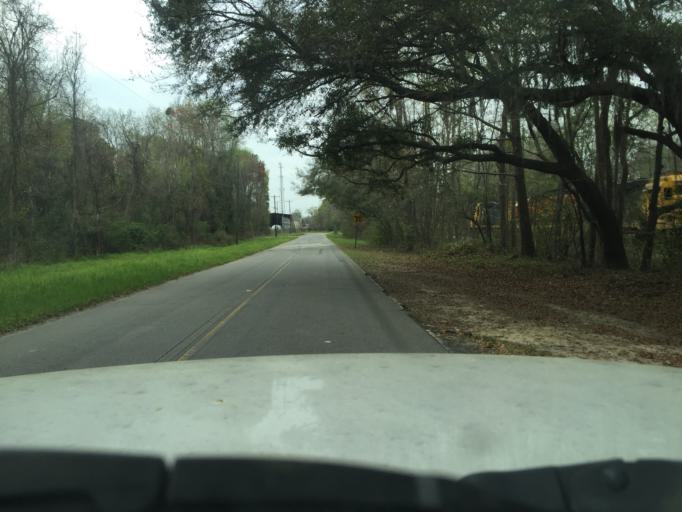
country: US
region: Georgia
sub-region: Chatham County
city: Garden City
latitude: 32.0756
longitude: -81.1502
